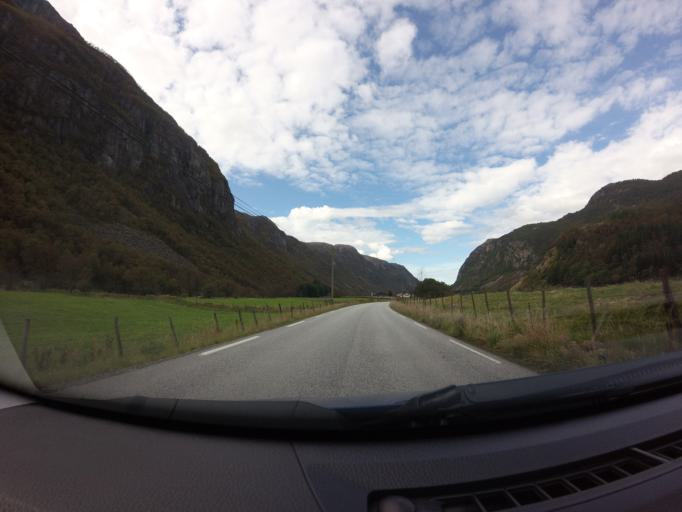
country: NO
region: Rogaland
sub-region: Forsand
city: Forsand
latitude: 58.8083
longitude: 6.2389
